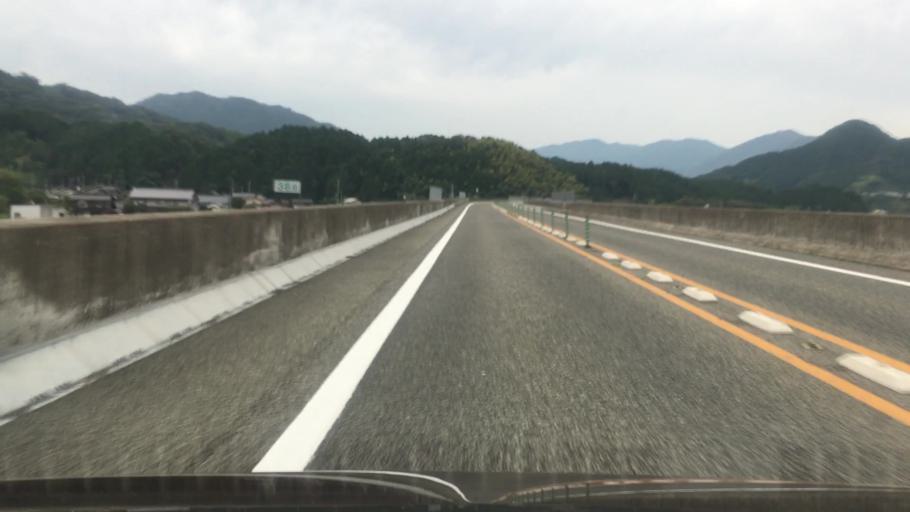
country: JP
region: Kyoto
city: Fukuchiyama
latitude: 35.3055
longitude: 134.8849
